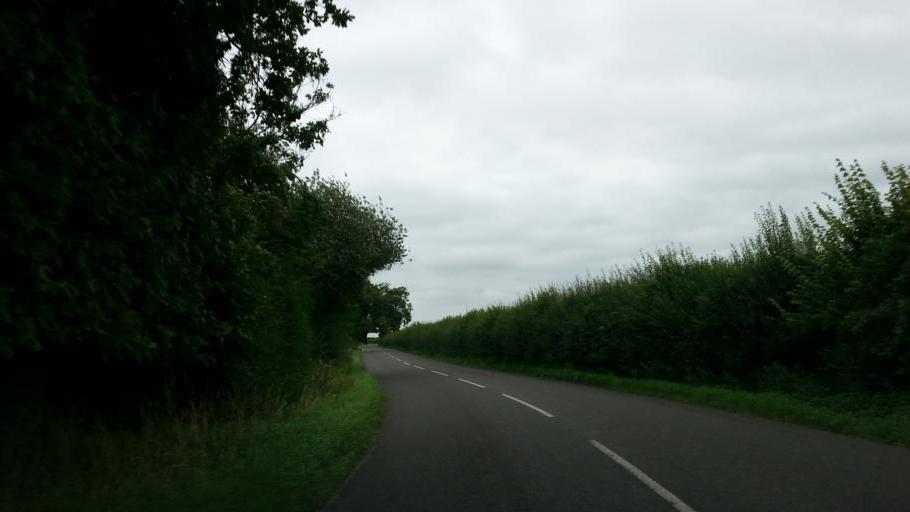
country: GB
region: England
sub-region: Nottinghamshire
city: Southwell
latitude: 53.1107
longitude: -0.9147
